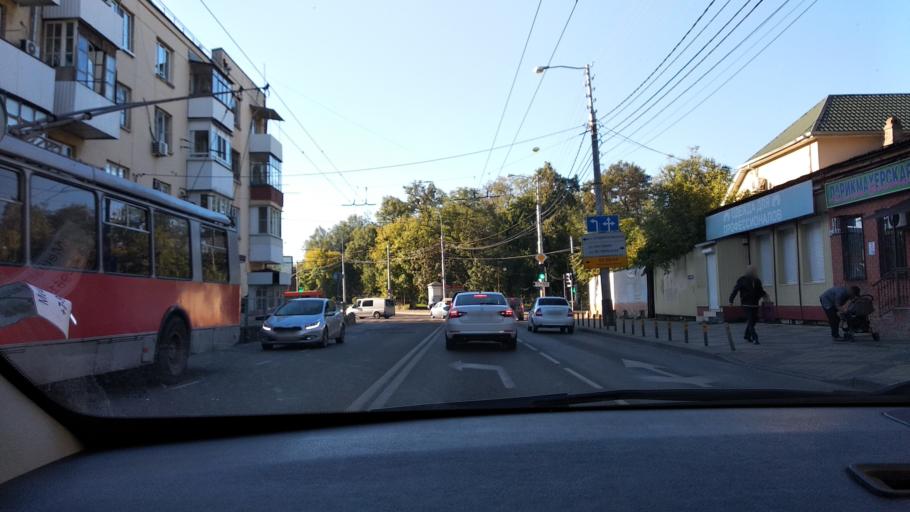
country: RU
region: Krasnodarskiy
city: Krasnodar
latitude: 45.0144
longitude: 38.9738
